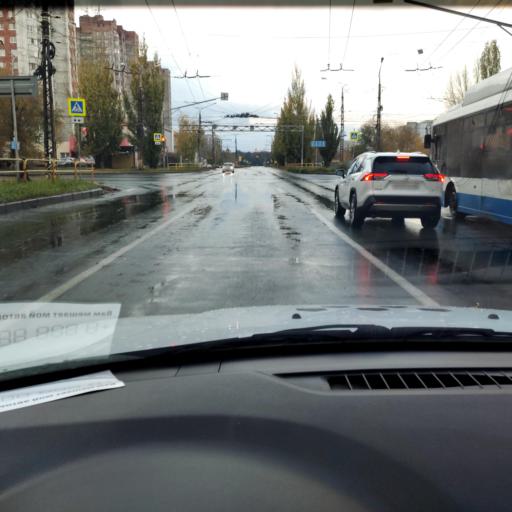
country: RU
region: Samara
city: Tol'yatti
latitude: 53.5103
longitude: 49.4305
